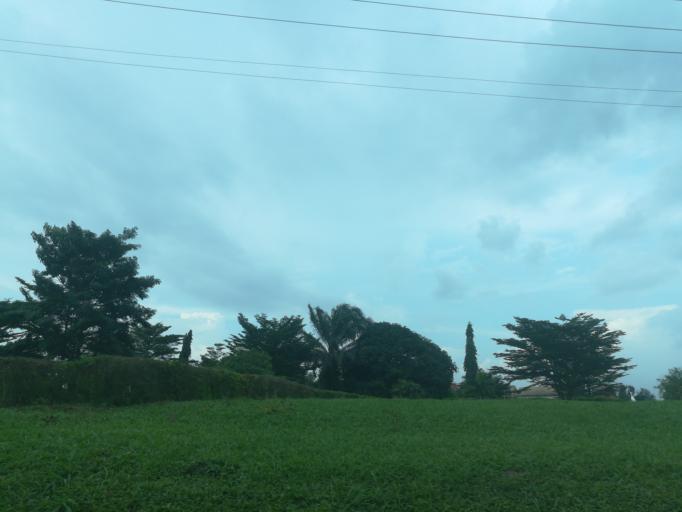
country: NG
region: Lagos
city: Ikorodu
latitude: 6.6352
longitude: 3.5237
